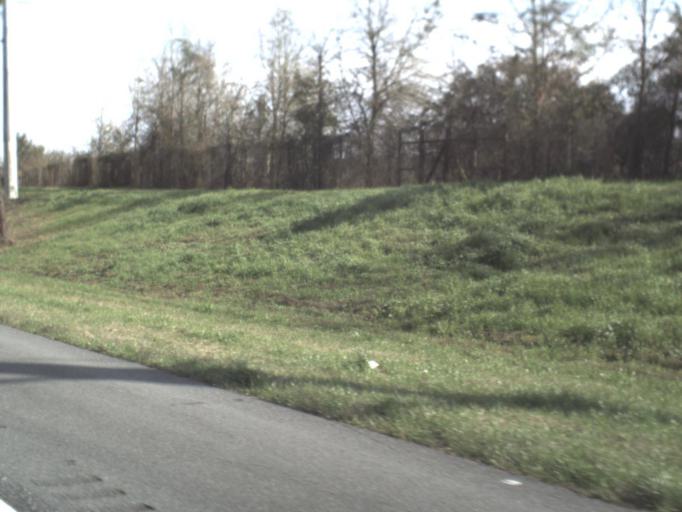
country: US
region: Florida
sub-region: Leon County
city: Tallahassee
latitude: 30.4983
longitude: -84.1809
